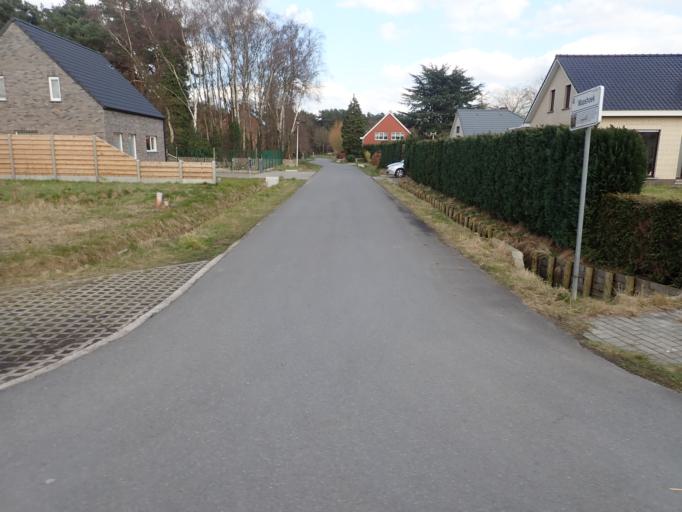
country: BE
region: Flanders
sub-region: Provincie Antwerpen
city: Vorselaar
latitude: 51.2179
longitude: 4.7585
